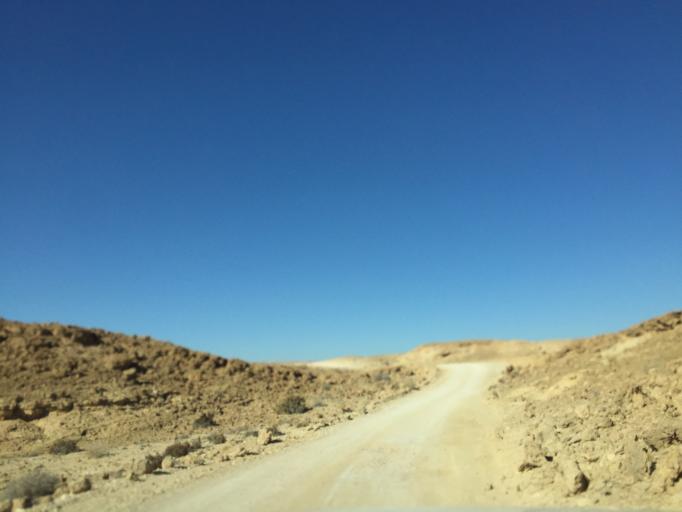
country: IL
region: Southern District
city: Mitzpe Ramon
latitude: 30.6126
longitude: 34.9334
